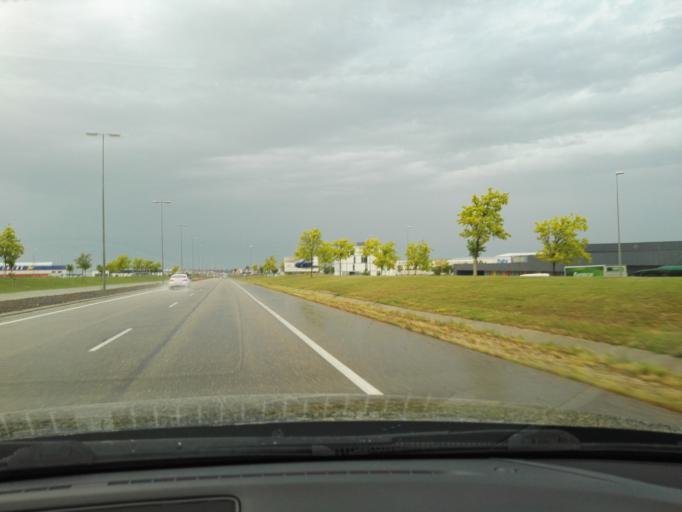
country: ES
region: Aragon
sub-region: Provincia de Zaragoza
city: Montecanal
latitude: 41.6428
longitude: -0.9940
